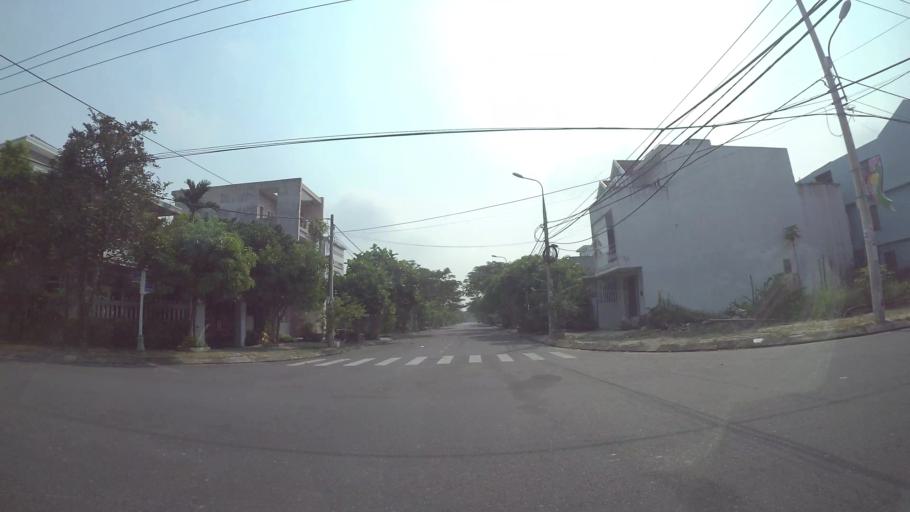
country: VN
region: Da Nang
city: Cam Le
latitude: 15.9963
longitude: 108.2133
